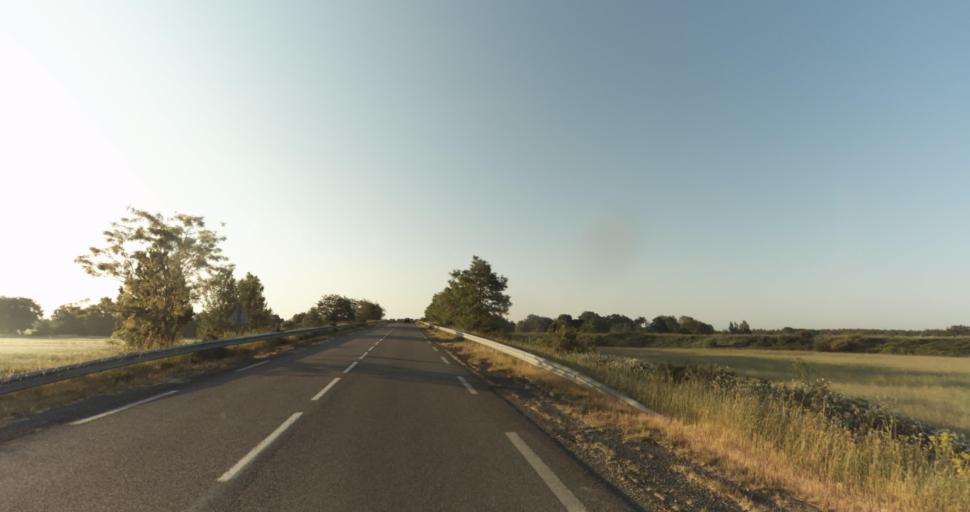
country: FR
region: Midi-Pyrenees
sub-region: Departement de la Haute-Garonne
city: Fontenilles
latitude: 43.5826
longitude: 1.2019
